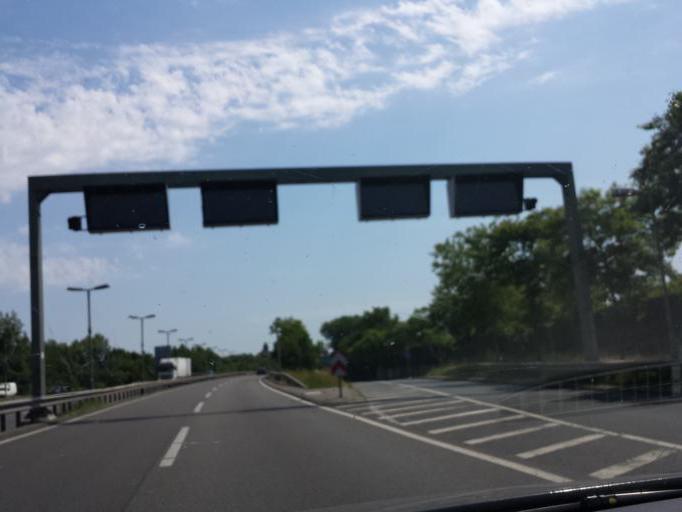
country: DE
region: Berlin
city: Tegel
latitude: 52.5972
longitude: 13.2840
